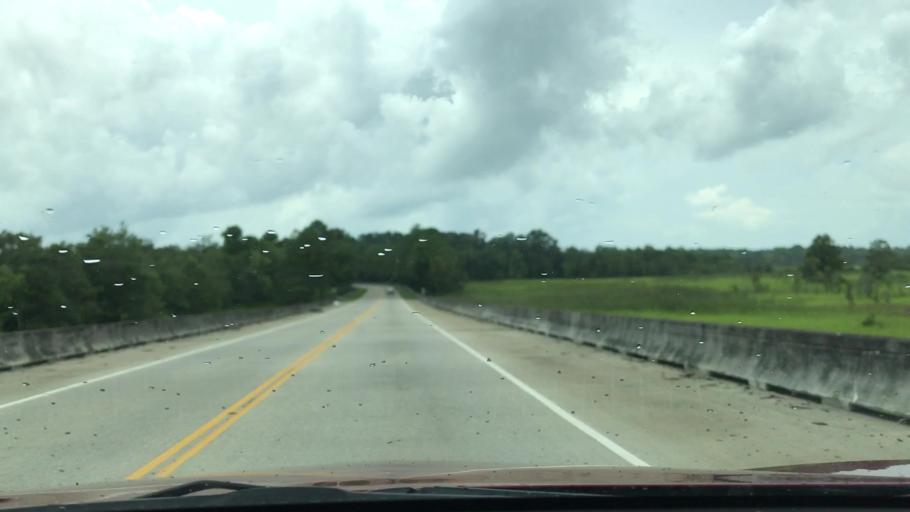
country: US
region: South Carolina
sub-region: Georgetown County
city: Georgetown
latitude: 33.4793
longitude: -79.2739
